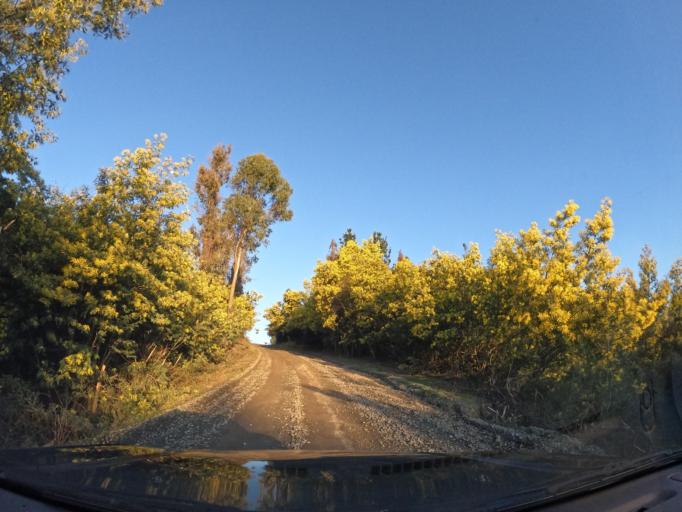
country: CL
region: Biobio
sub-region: Provincia de Concepcion
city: Chiguayante
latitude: -37.0115
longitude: -72.8686
